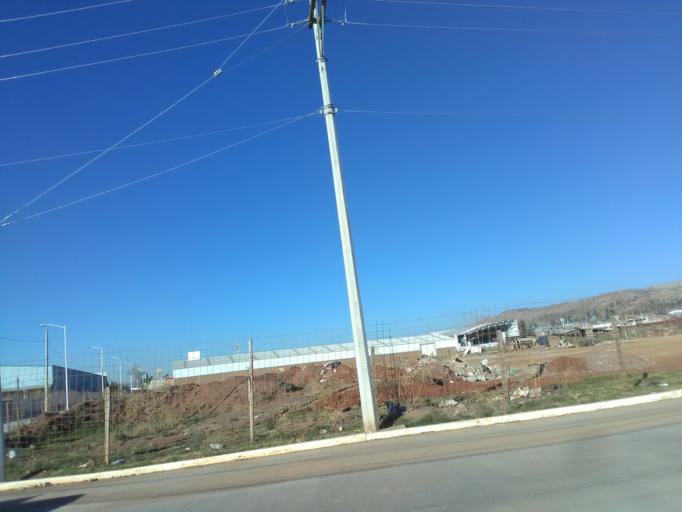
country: MX
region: Durango
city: Victoria de Durango
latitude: 24.0541
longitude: -104.6499
